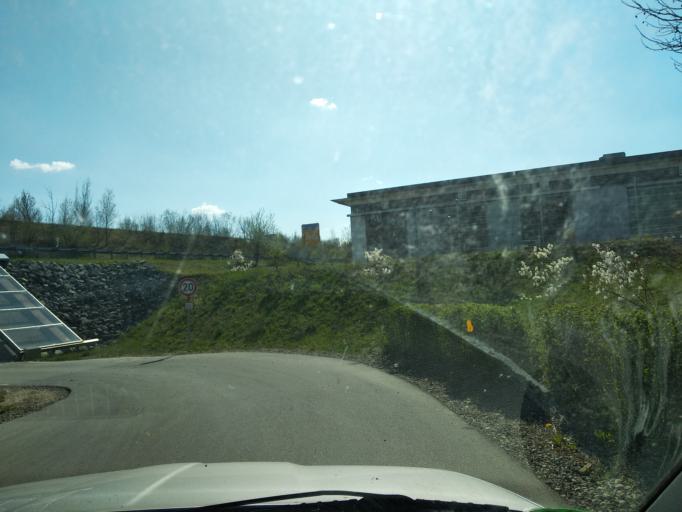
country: DE
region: Bavaria
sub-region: Swabia
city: Erkheim
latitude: 48.0301
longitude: 10.3350
